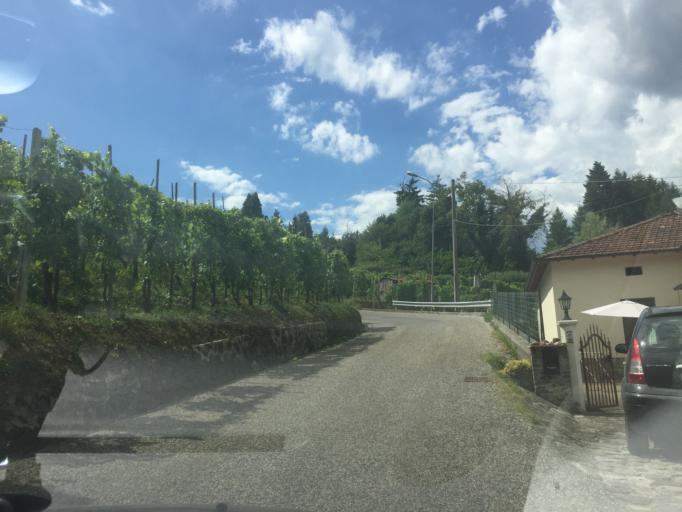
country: IT
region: Tuscany
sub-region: Provincia di Lucca
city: Castelnuovo di Garfagnana
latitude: 44.1189
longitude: 10.3938
